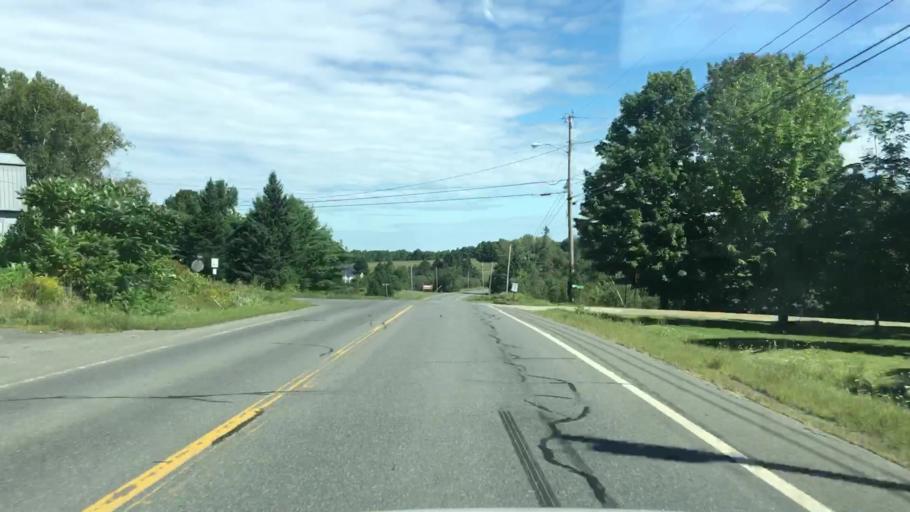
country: US
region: Maine
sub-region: Penobscot County
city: Dexter
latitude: 45.0699
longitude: -69.2384
